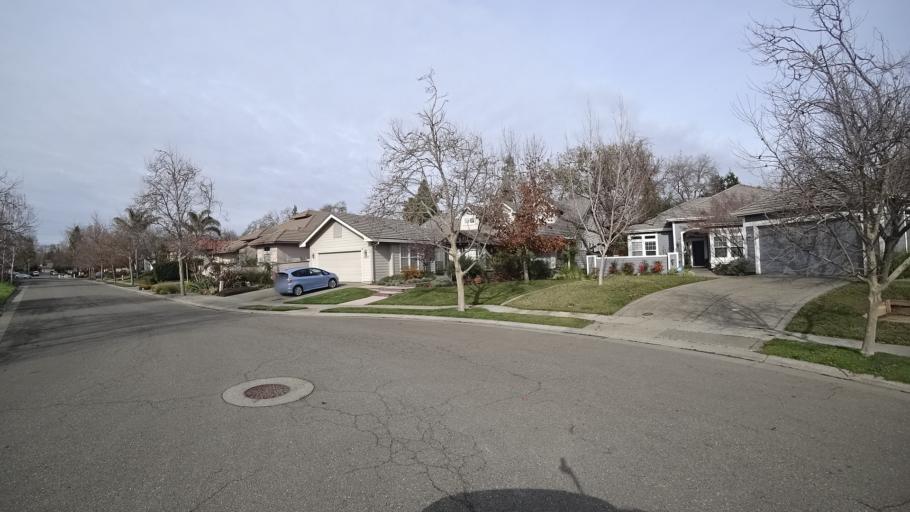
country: US
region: California
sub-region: Yolo County
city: Davis
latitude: 38.5454
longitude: -121.6989
